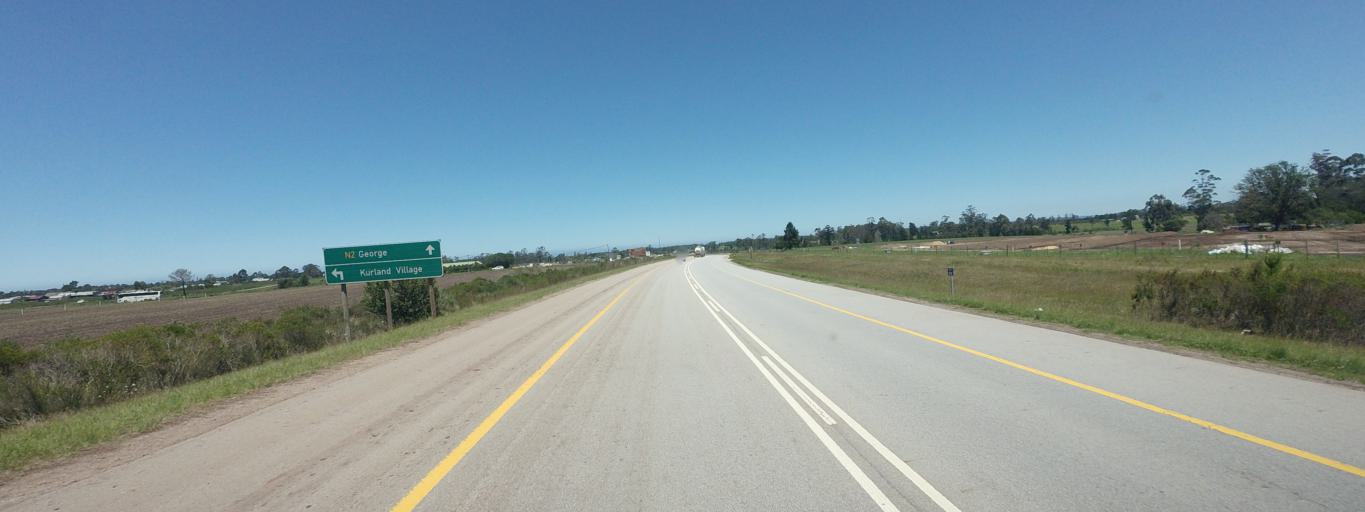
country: ZA
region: Western Cape
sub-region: Eden District Municipality
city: Plettenberg Bay
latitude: -33.9443
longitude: 23.4871
